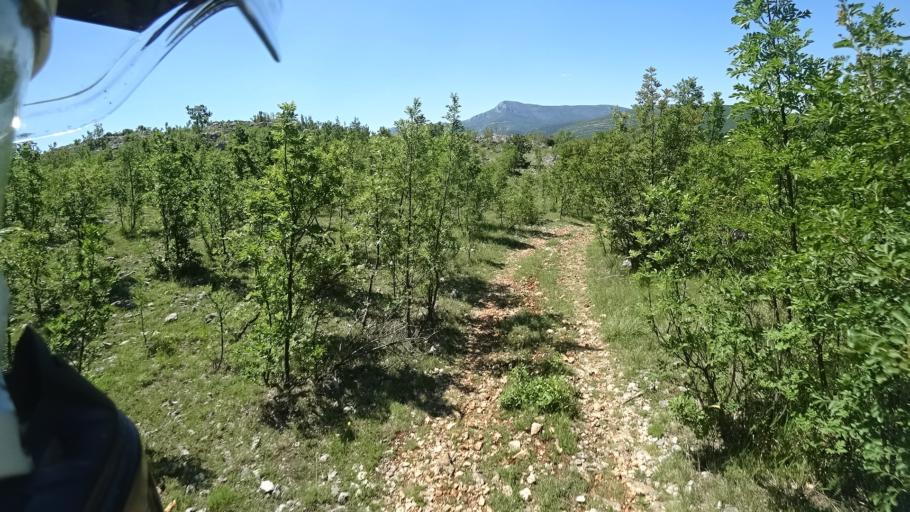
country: BA
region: Federation of Bosnia and Herzegovina
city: Bosansko Grahovo
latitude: 44.0174
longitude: 16.3609
